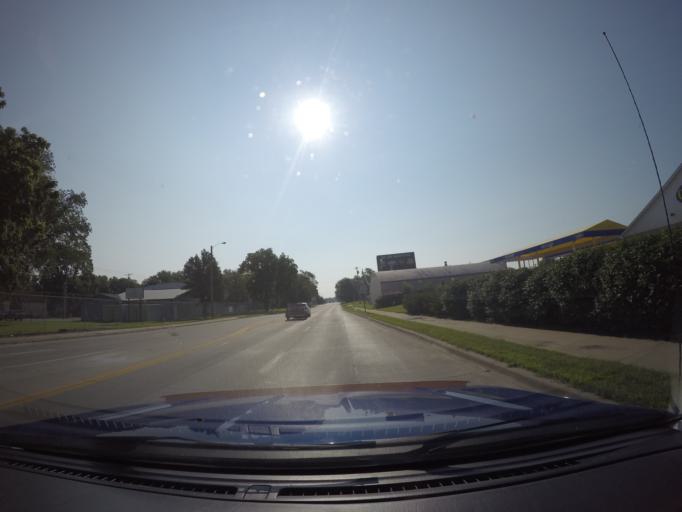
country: US
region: Kansas
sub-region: Riley County
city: Manhattan
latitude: 39.1742
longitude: -96.5714
